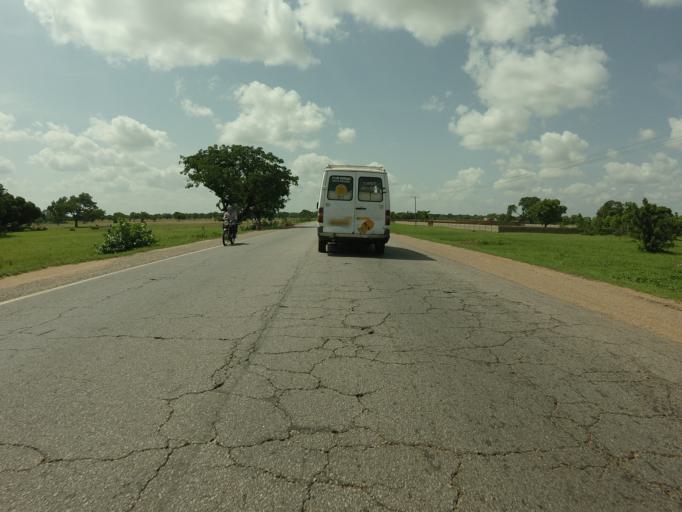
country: GH
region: Northern
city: Savelugu
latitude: 9.5653
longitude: -0.8358
